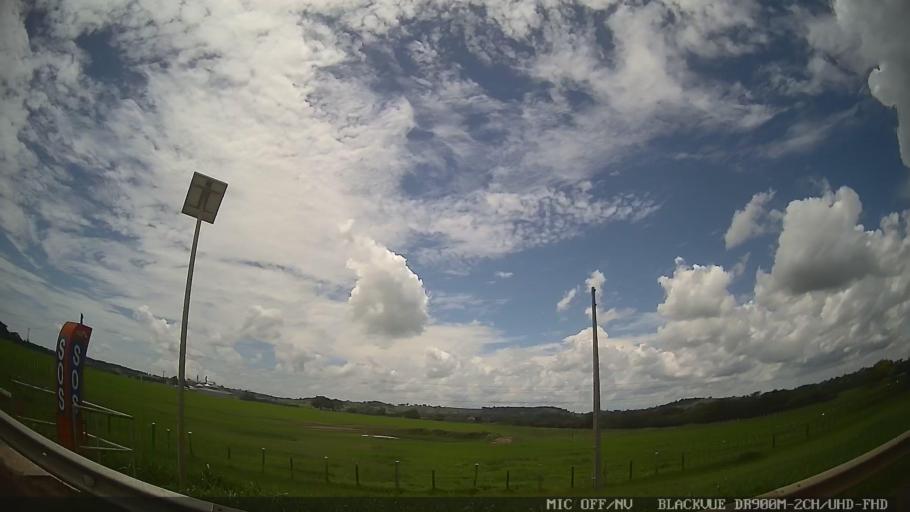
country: BR
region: Sao Paulo
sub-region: Conchas
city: Conchas
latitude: -23.0445
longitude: -47.9409
